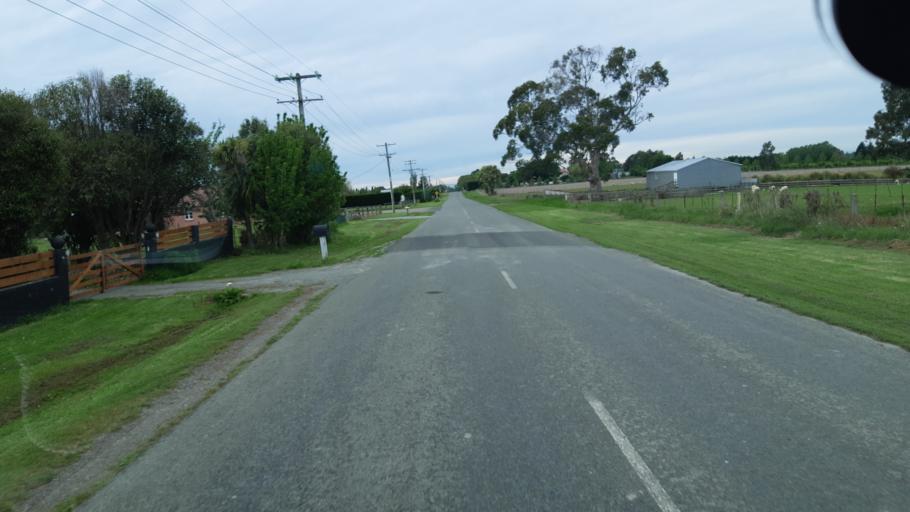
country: NZ
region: Canterbury
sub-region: Timaru District
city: Timaru
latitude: -44.4108
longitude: 171.1821
